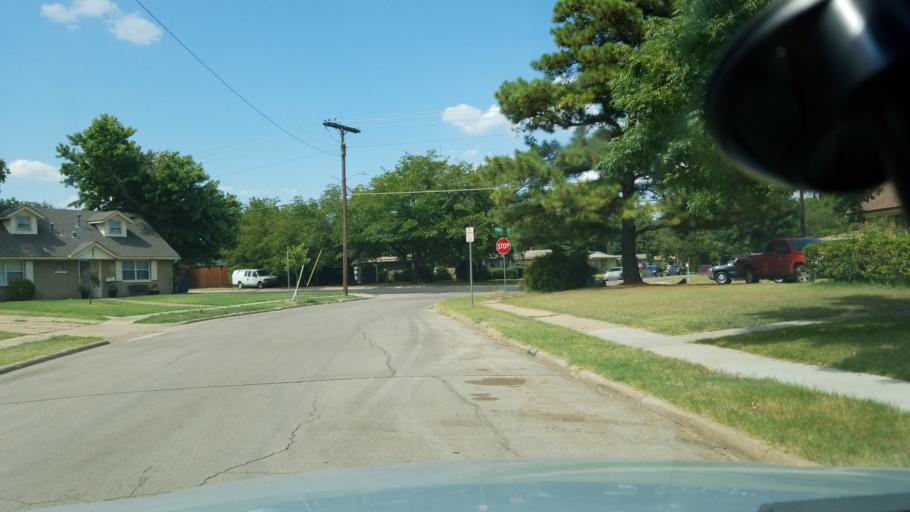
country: US
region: Texas
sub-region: Dallas County
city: Irving
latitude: 32.8229
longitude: -96.9786
